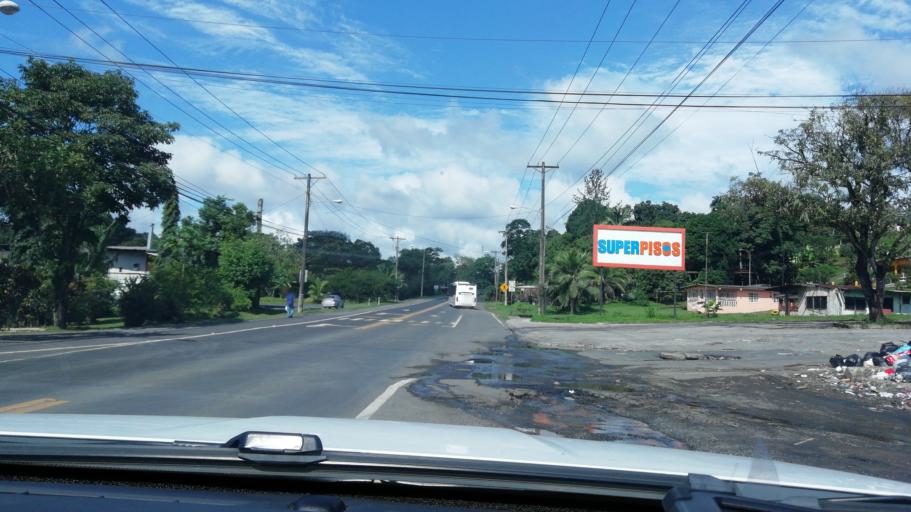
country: PA
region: Panama
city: Chilibre
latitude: 9.1224
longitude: -79.5990
